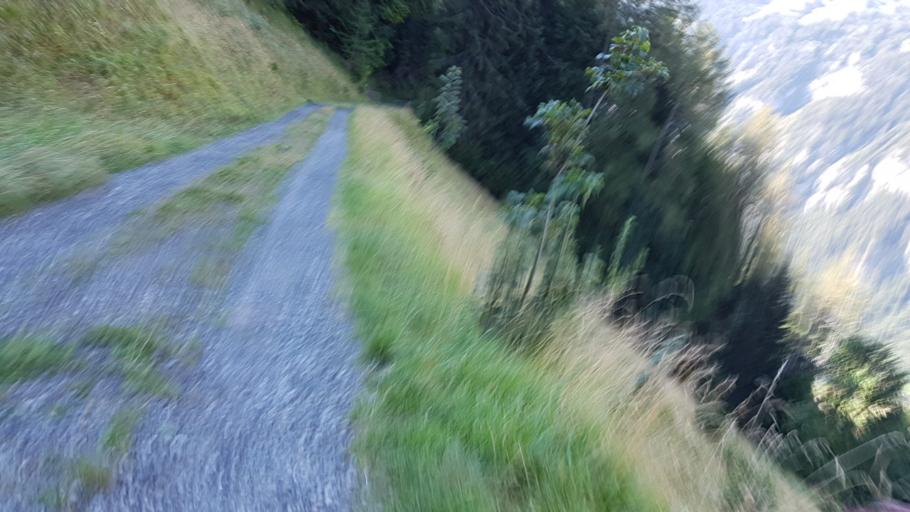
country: CH
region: Bern
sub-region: Frutigen-Niedersimmental District
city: Kandersteg
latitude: 46.5424
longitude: 7.6733
